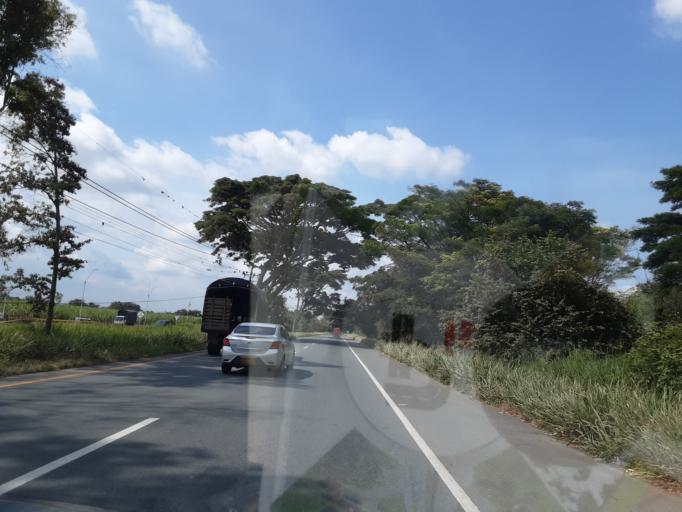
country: CO
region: Valle del Cauca
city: Guacari
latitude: 3.7464
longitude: -76.3249
